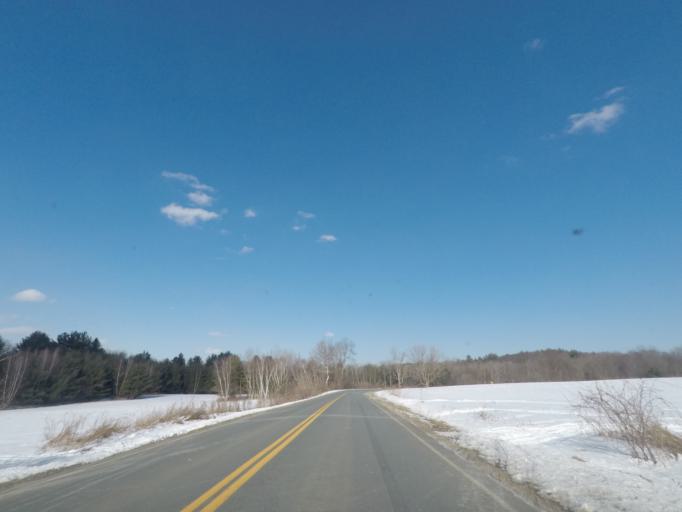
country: US
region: New York
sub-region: Saratoga County
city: Stillwater
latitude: 42.8685
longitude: -73.5904
